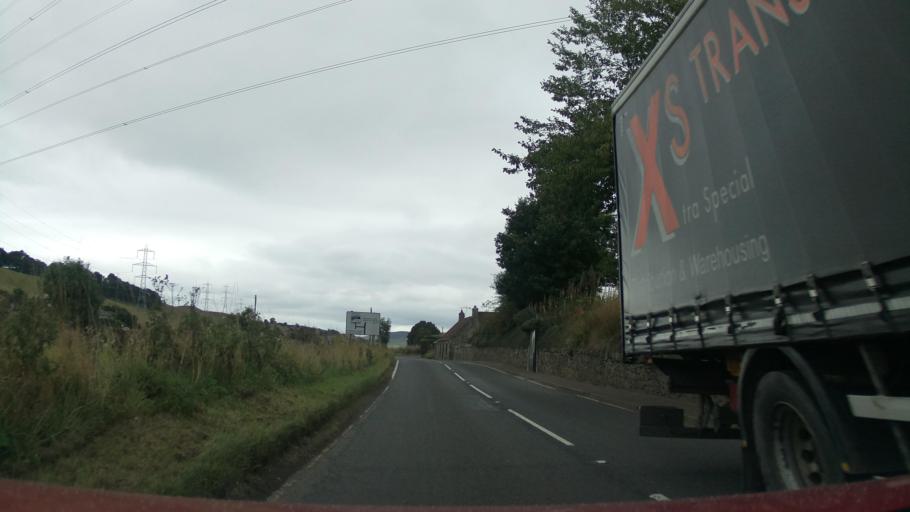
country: GB
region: Scotland
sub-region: Fife
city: Kinglassie
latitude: 56.1973
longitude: -3.2588
